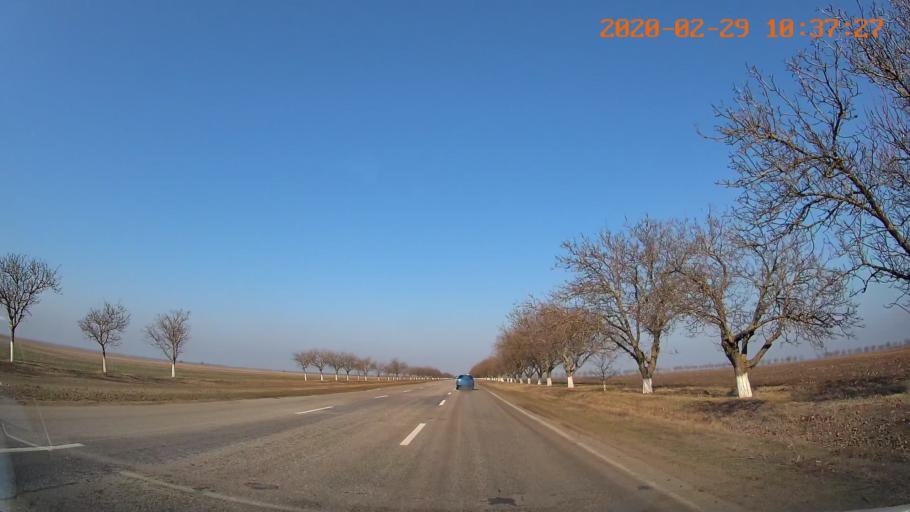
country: MD
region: Anenii Noi
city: Varnita
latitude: 47.0060
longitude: 29.4896
